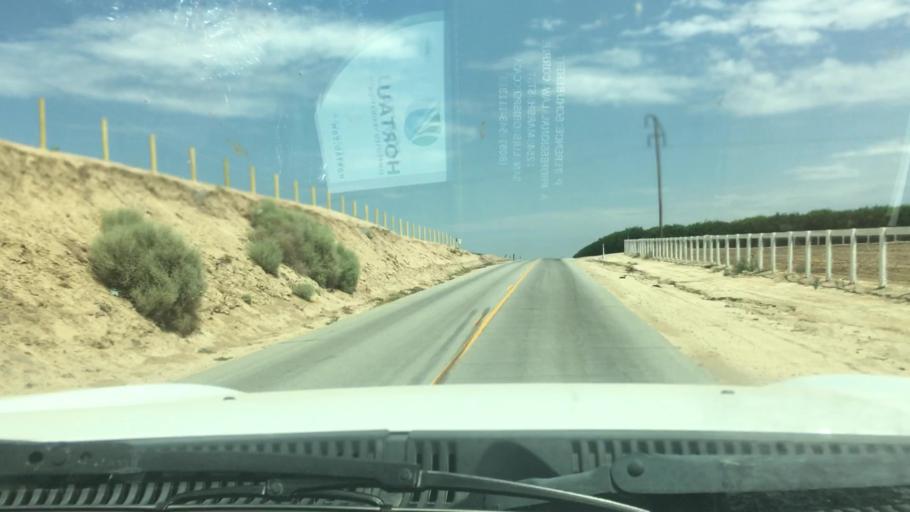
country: US
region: California
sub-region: Kern County
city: McFarland
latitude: 35.5662
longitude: -119.1511
